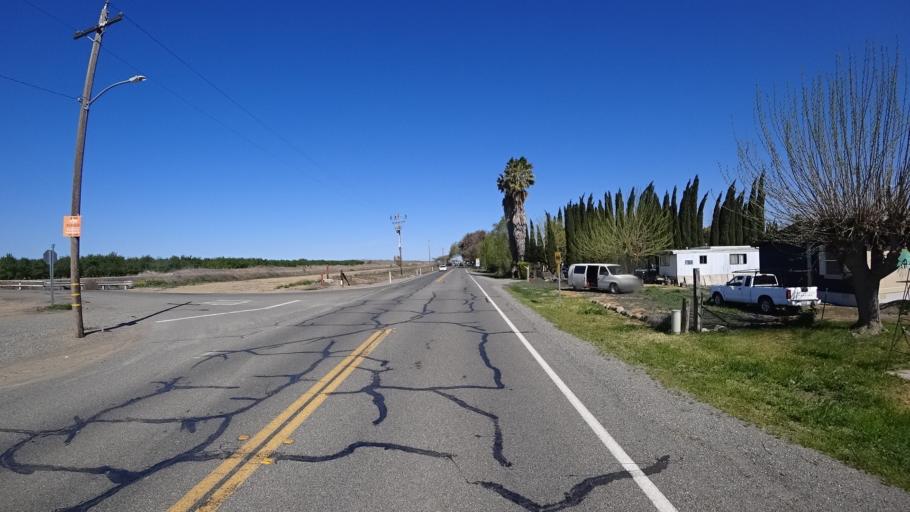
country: US
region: California
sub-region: Glenn County
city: Hamilton City
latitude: 39.7375
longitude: -122.0160
